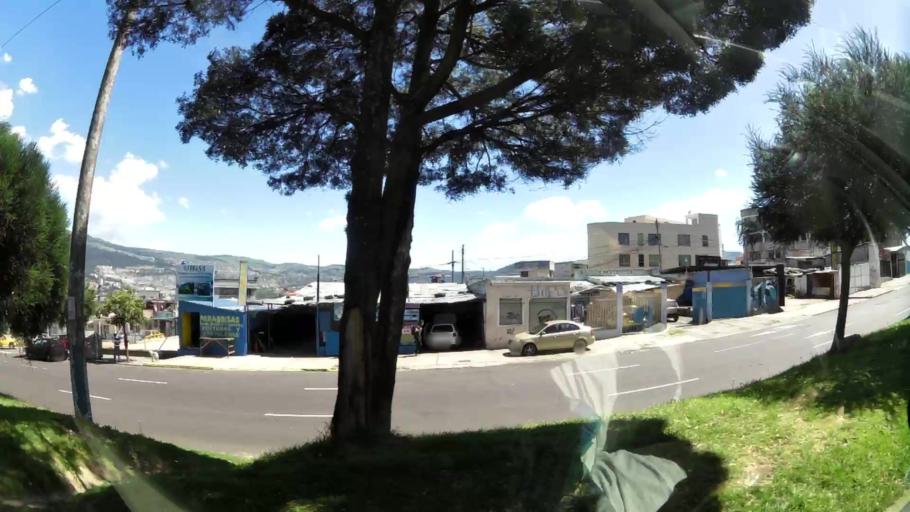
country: EC
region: Pichincha
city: Quito
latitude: -0.1054
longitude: -78.4837
